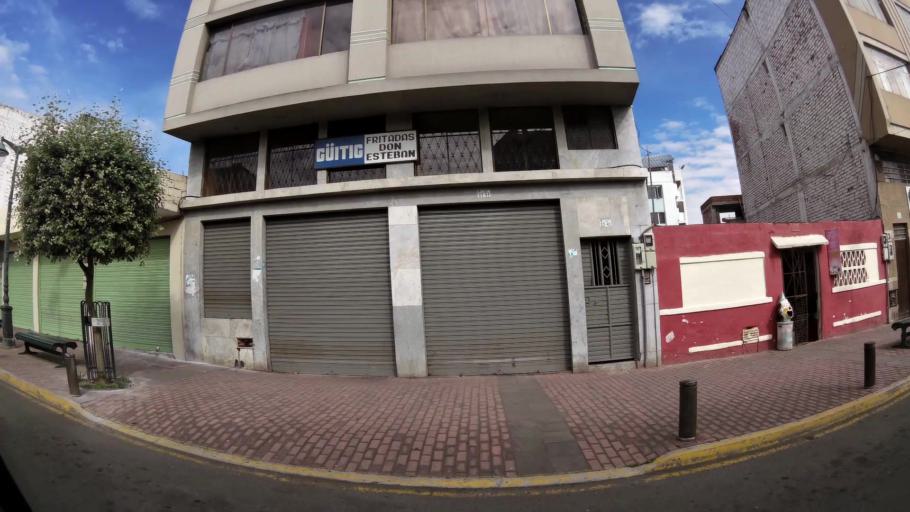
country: EC
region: Tungurahua
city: Ambato
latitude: -1.2319
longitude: -78.6292
